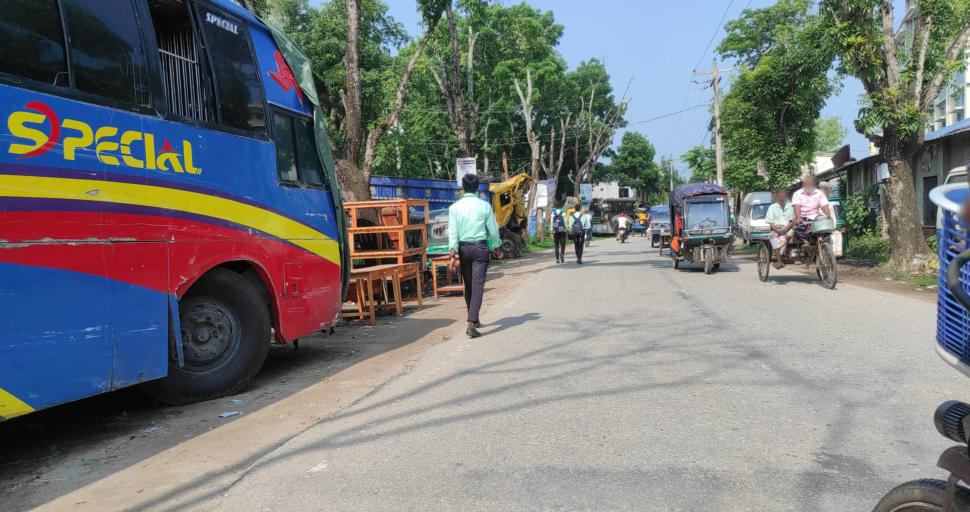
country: BD
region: Rajshahi
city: Ishurdi
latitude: 24.2903
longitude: 89.0782
